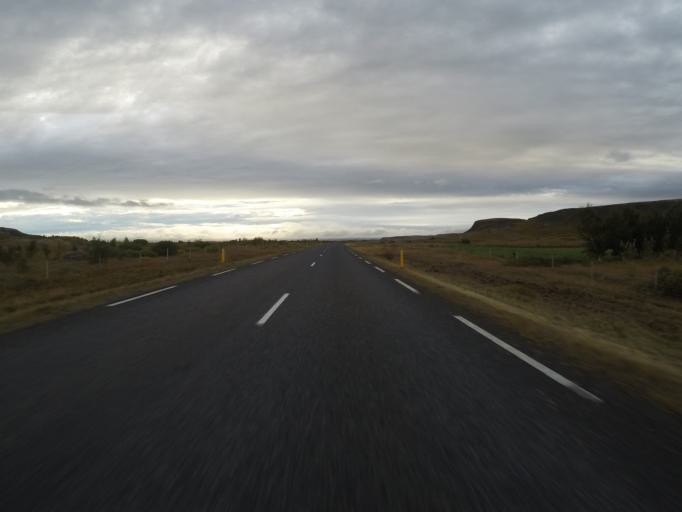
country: IS
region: South
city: Vestmannaeyjar
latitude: 64.0416
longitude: -20.1982
